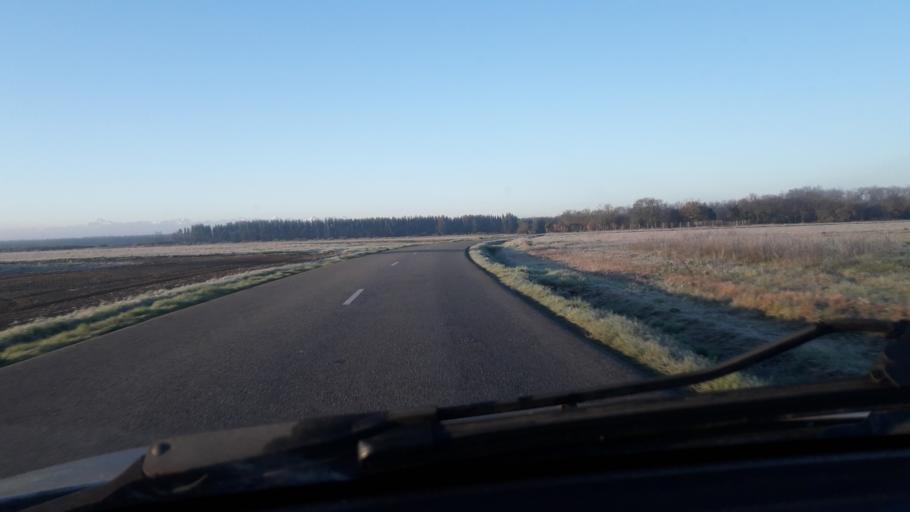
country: FR
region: Midi-Pyrenees
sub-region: Departement de la Haute-Garonne
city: Longages
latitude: 43.3552
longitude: 1.2184
